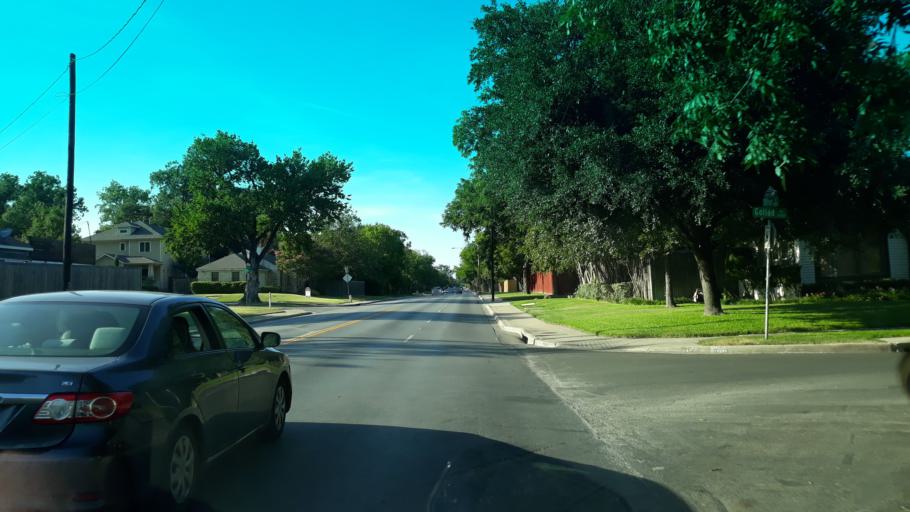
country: US
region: Texas
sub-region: Dallas County
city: Highland Park
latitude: 32.8180
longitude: -96.7616
